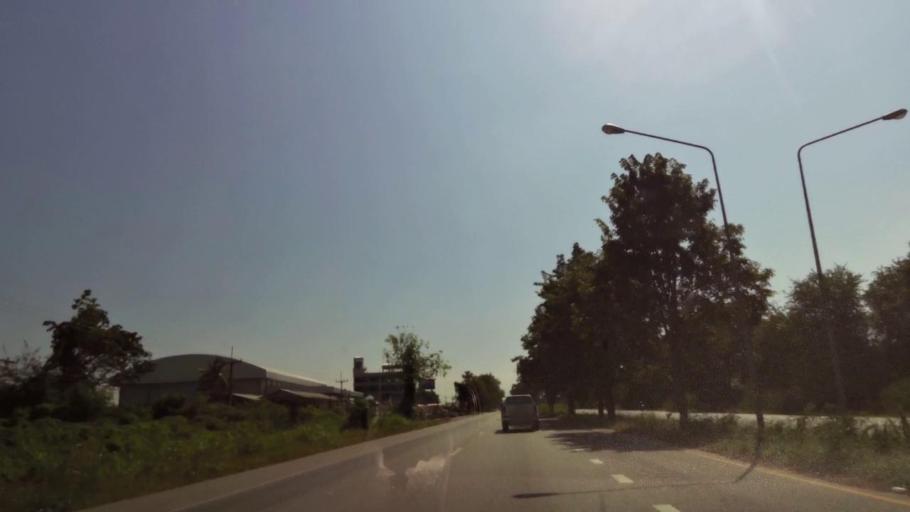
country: TH
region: Nakhon Sawan
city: Kao Liao
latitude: 15.8383
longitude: 100.1175
